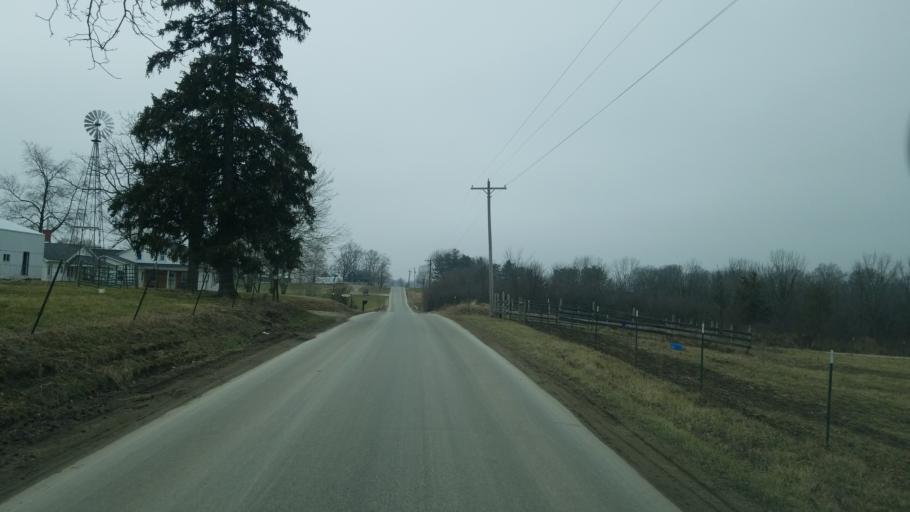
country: US
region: Indiana
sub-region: Adams County
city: Geneva
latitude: 40.6149
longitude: -84.9160
